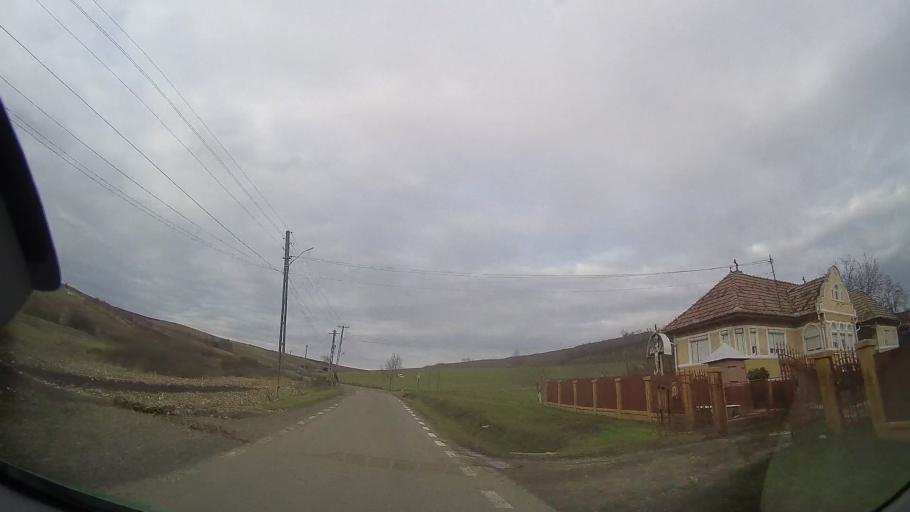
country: RO
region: Mures
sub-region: Comuna Cozma
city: Cozma
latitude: 46.8165
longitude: 24.4933
